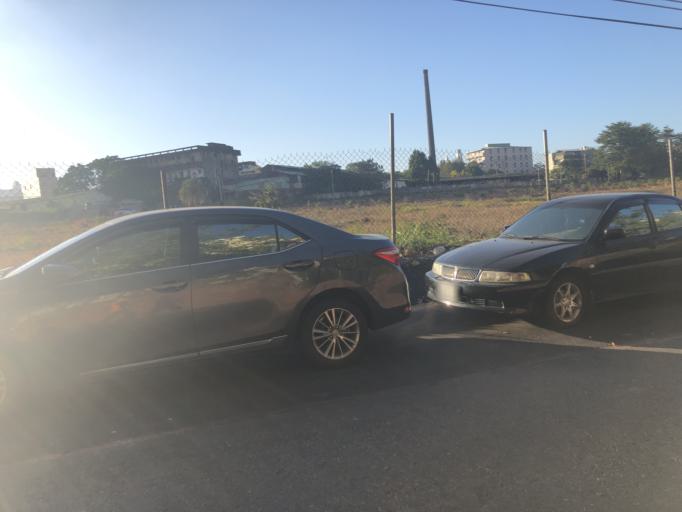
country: TW
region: Taiwan
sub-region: Taichung City
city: Taichung
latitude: 24.1370
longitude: 120.6070
